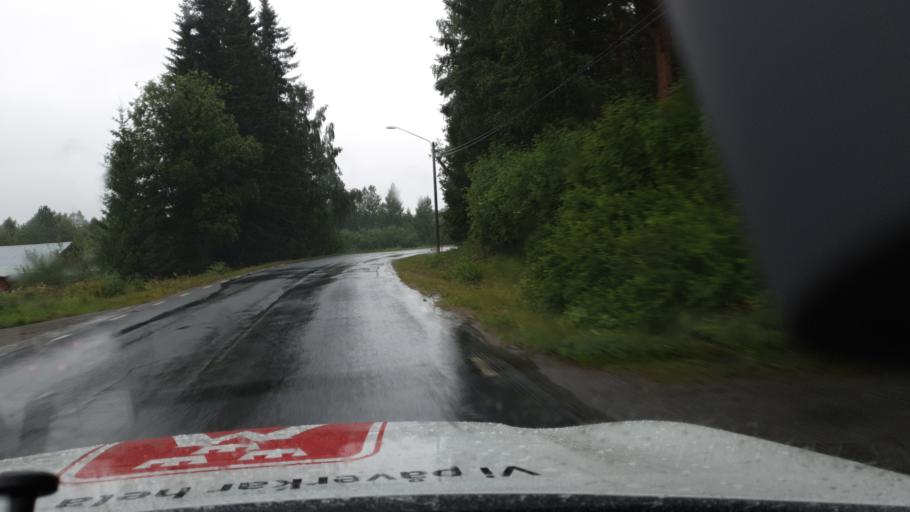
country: SE
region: Vaesterbotten
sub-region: Skelleftea Kommun
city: Soedra Bergsbyn
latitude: 64.5811
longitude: 21.0062
